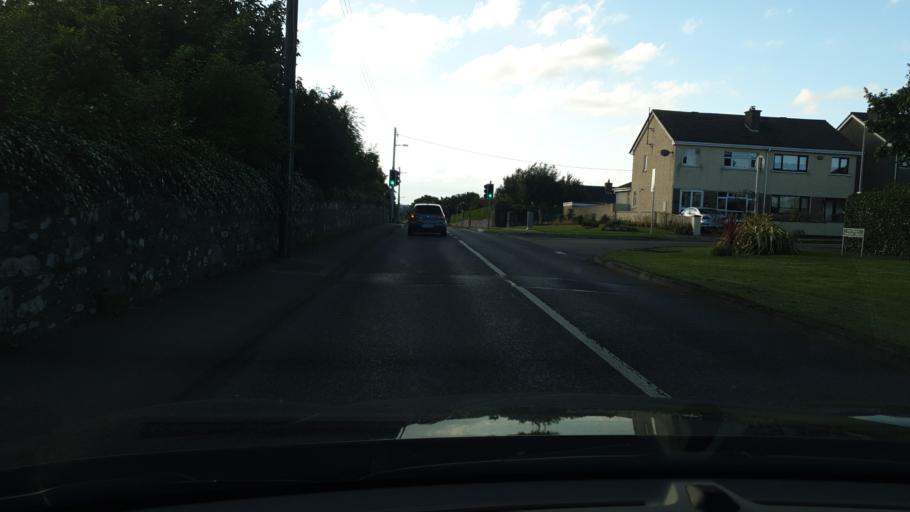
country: IE
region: Leinster
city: Balbriggan
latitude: 53.6053
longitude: -6.1711
